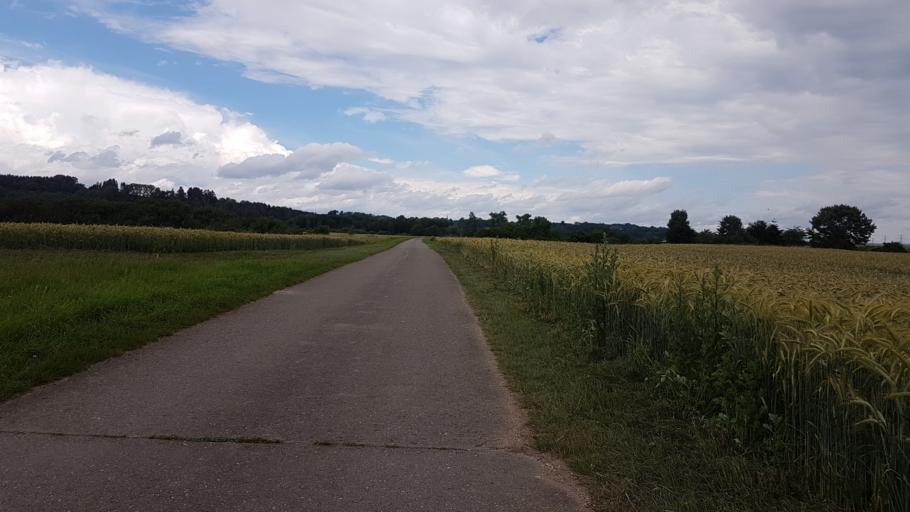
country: DE
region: Baden-Wuerttemberg
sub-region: Tuebingen Region
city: Herbertingen
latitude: 48.0933
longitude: 9.4207
